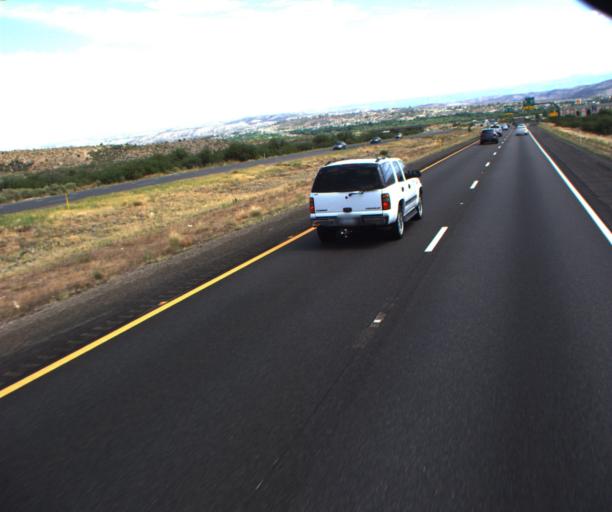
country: US
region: Arizona
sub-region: Yavapai County
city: Camp Verde
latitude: 34.5710
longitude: -111.8910
